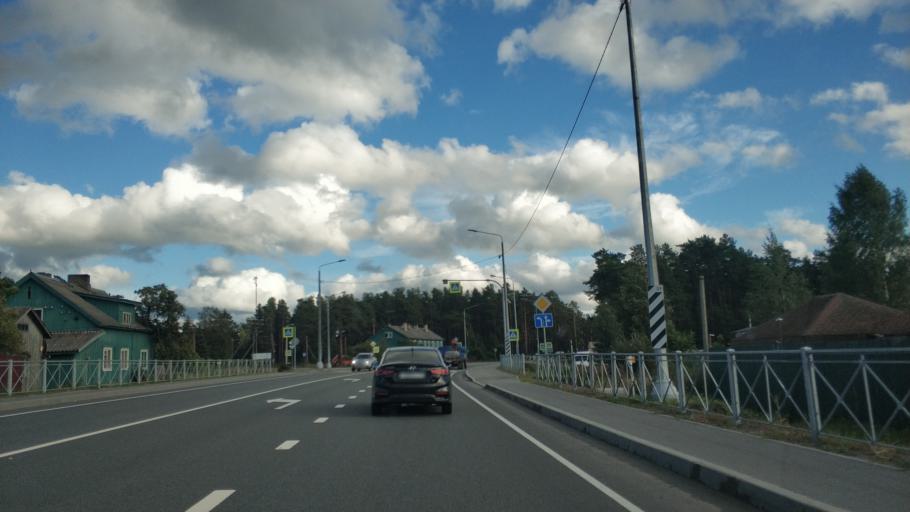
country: RU
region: Leningrad
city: Priozersk
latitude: 61.0060
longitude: 30.1781
